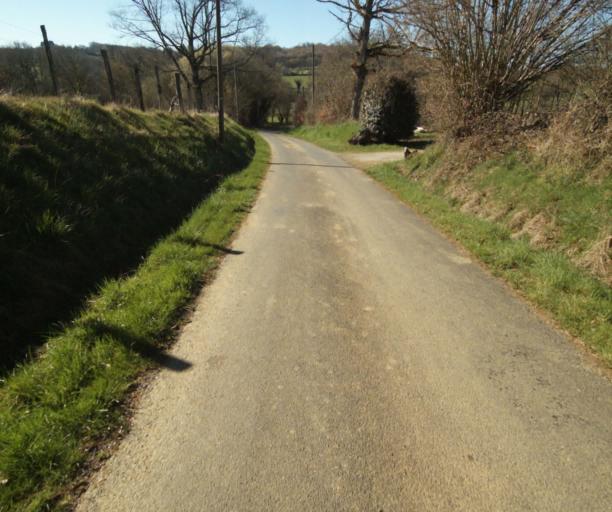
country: FR
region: Limousin
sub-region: Departement de la Correze
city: Chamboulive
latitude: 45.4204
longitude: 1.7091
